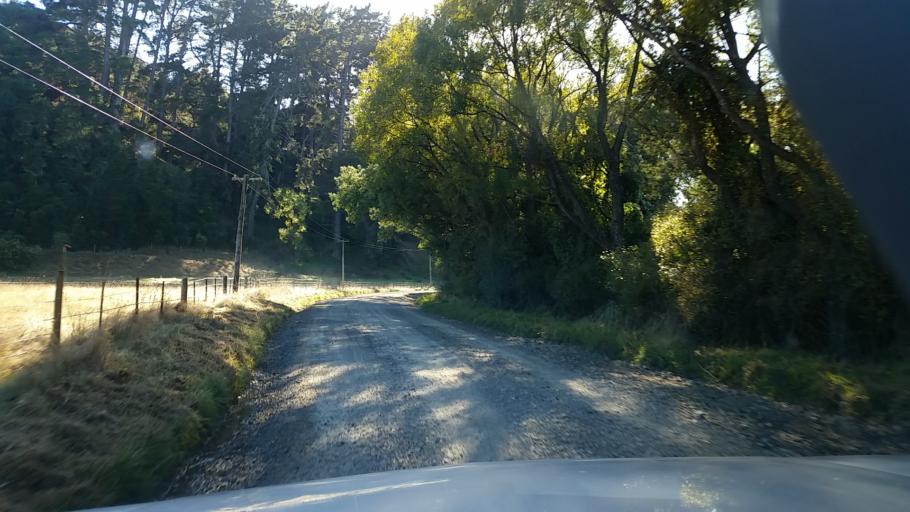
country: NZ
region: Marlborough
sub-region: Marlborough District
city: Blenheim
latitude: -41.4510
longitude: 173.8721
